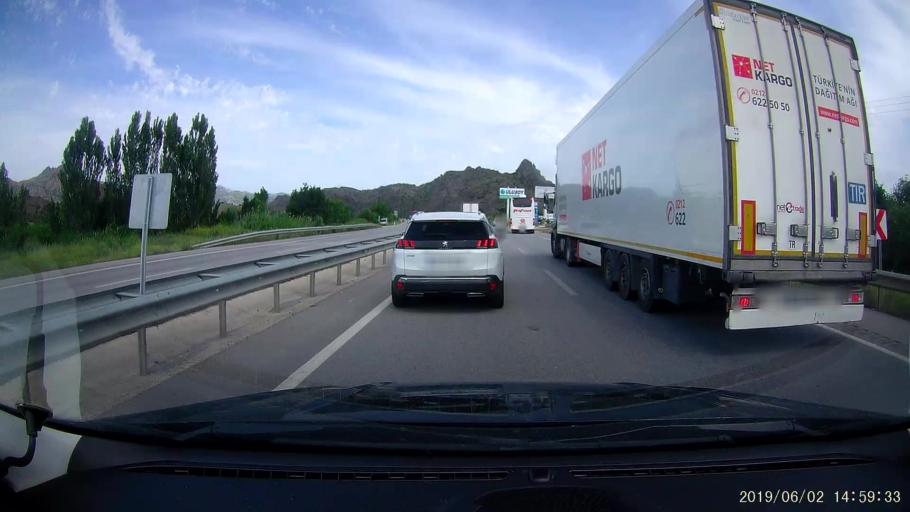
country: TR
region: Corum
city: Osmancik
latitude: 40.9714
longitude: 34.6975
